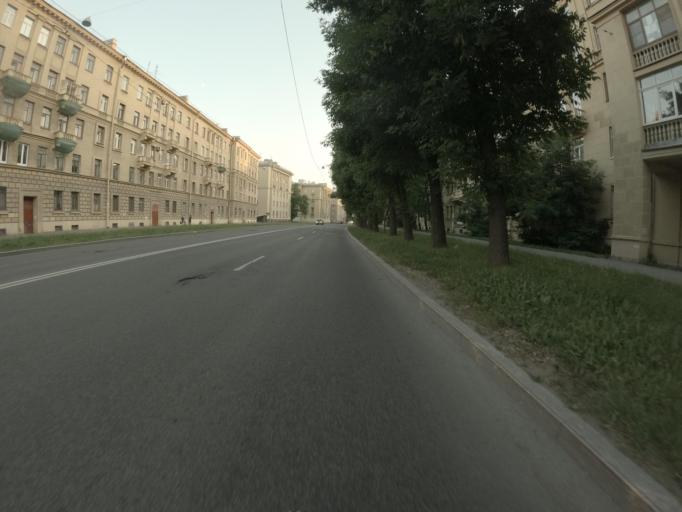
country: RU
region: St.-Petersburg
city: Avtovo
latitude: 59.8716
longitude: 30.2653
